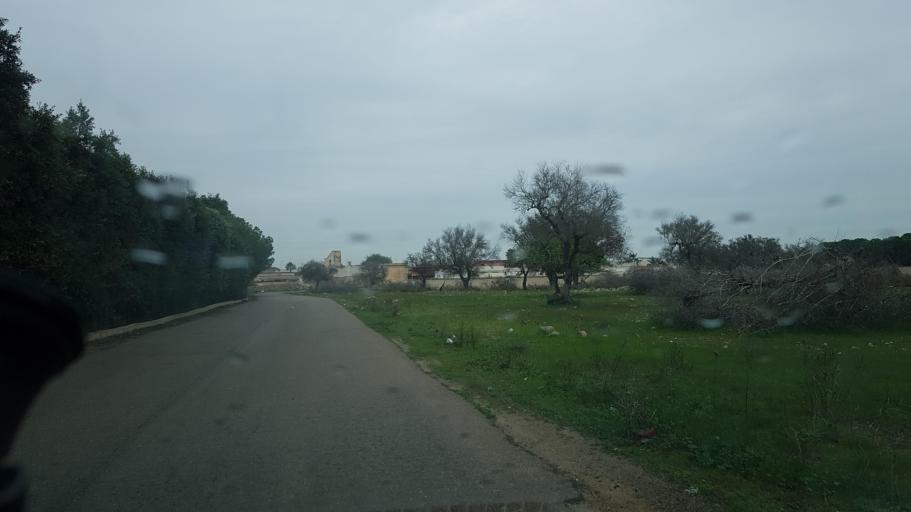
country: IT
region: Apulia
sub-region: Provincia di Lecce
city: Leverano
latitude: 40.2775
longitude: 17.9867
